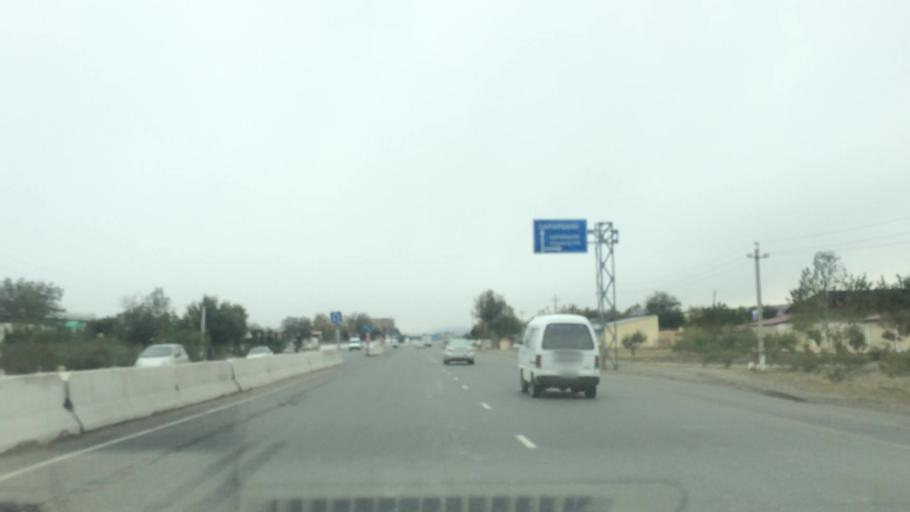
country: UZ
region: Samarqand
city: Jomboy
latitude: 39.7005
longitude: 67.0760
